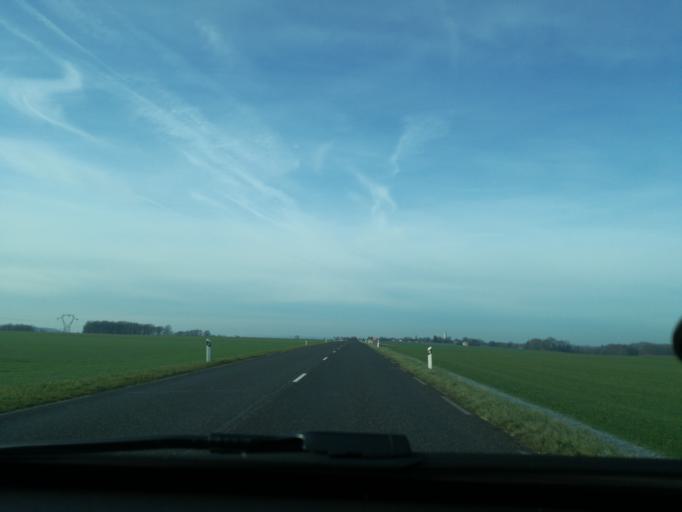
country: FR
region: Lorraine
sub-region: Departement de la Meuse
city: Revigny-sur-Ornain
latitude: 48.8306
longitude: 5.0664
